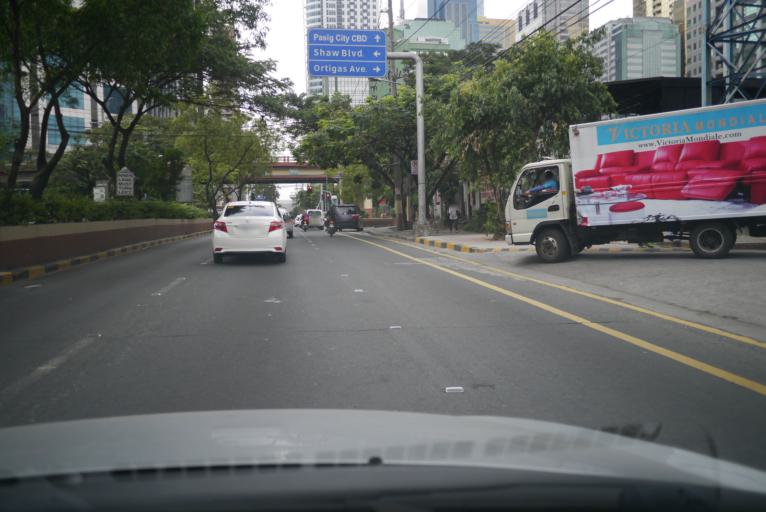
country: PH
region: Metro Manila
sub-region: Pasig
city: Pasig City
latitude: 14.5844
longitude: 121.0648
